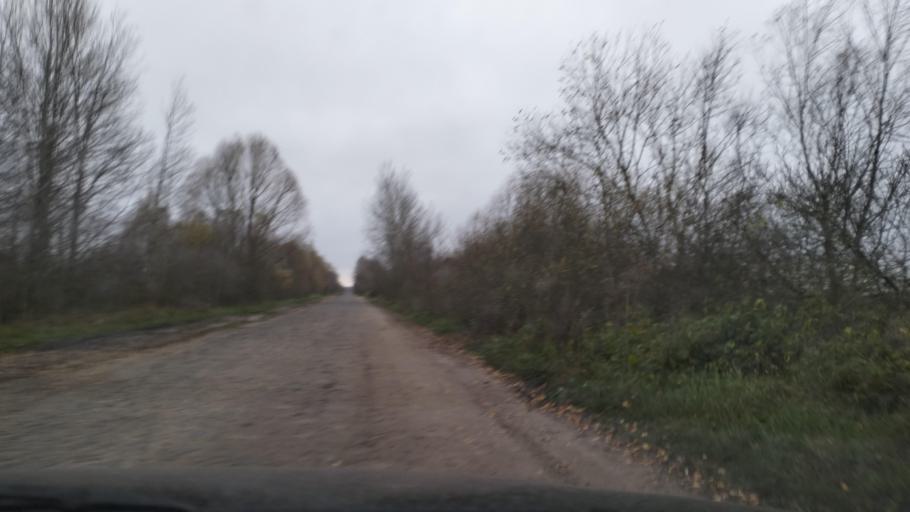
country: BY
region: Brest
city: Davyd-Haradok
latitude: 51.9906
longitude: 27.2056
